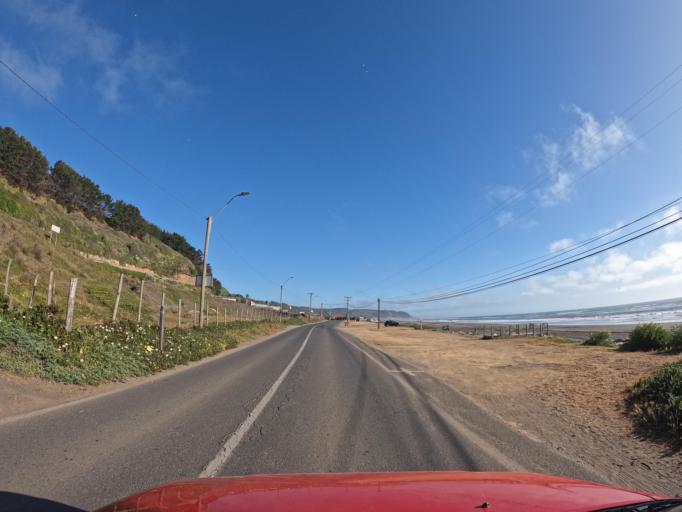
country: CL
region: Maule
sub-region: Provincia de Talca
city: Constitucion
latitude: -34.9158
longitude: -72.1820
